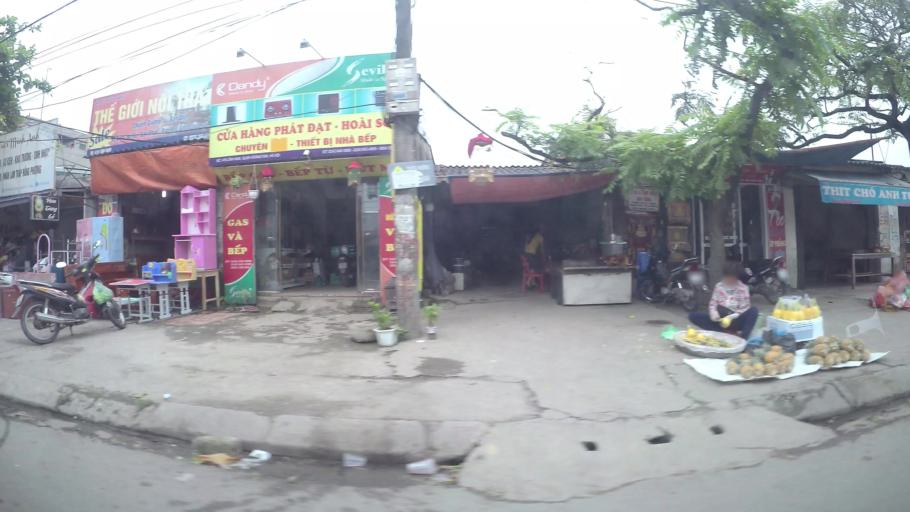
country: VN
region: Ha Noi
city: Hai BaTrung
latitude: 20.9809
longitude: 105.8822
